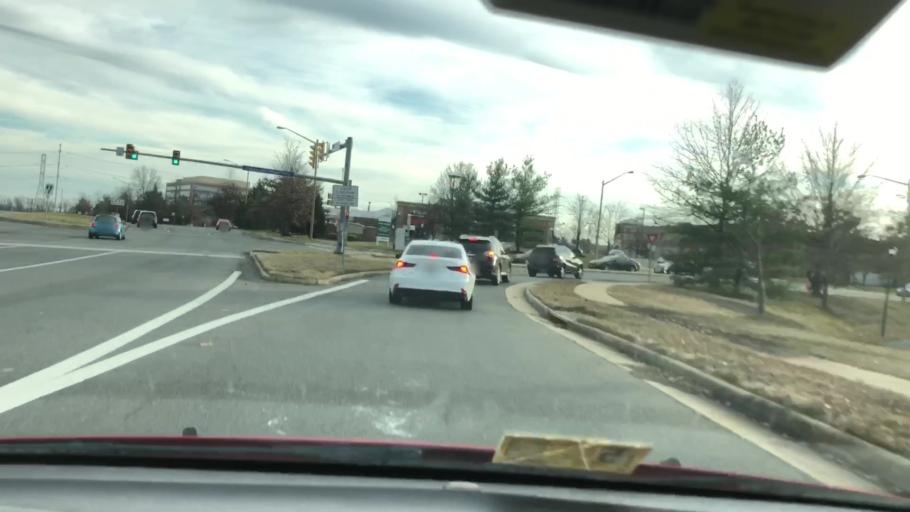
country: US
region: Virginia
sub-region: Fairfax County
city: Franconia
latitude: 38.7756
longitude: -77.1353
